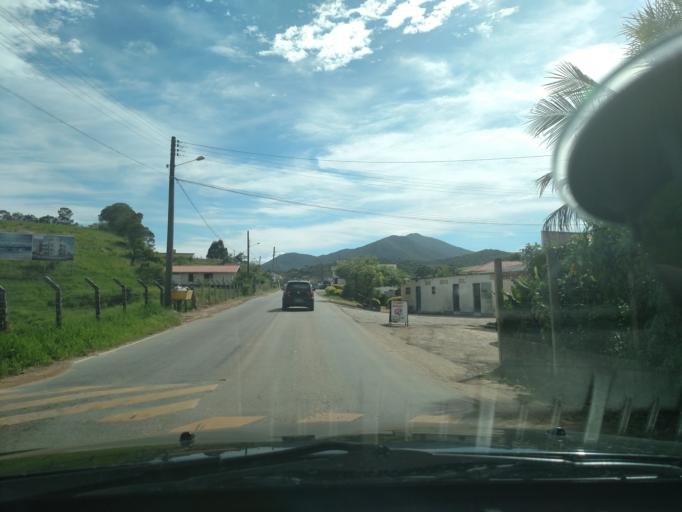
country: BR
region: Santa Catarina
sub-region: Biguacu
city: Biguacu
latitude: -27.3771
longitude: -48.6134
